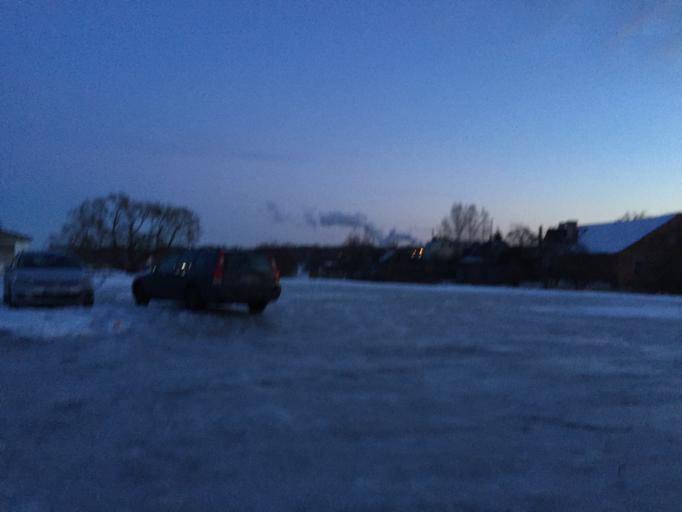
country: LV
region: Jaunjelgava
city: Jaunjelgava
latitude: 56.6206
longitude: 25.0883
